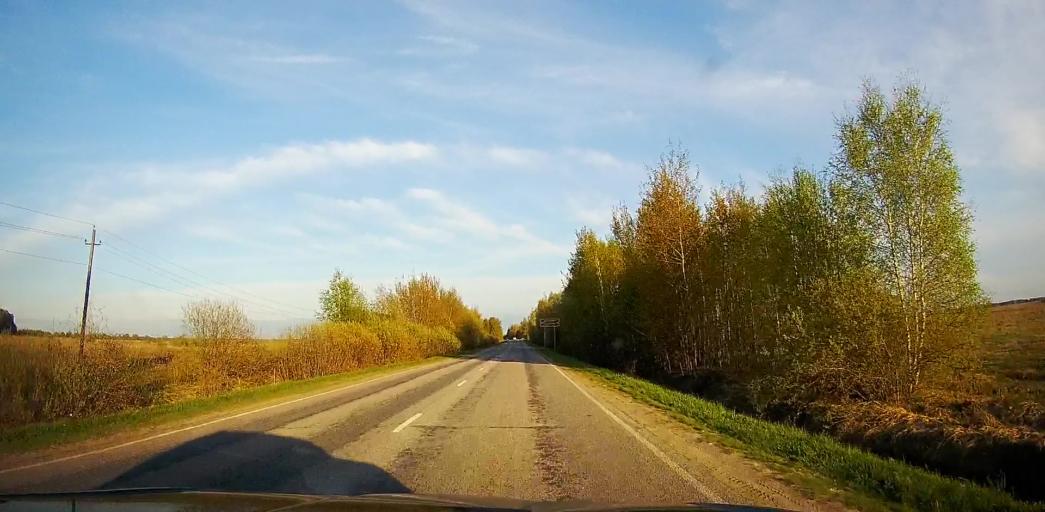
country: RU
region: Moskovskaya
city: Bronnitsy
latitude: 55.2774
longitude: 38.2215
